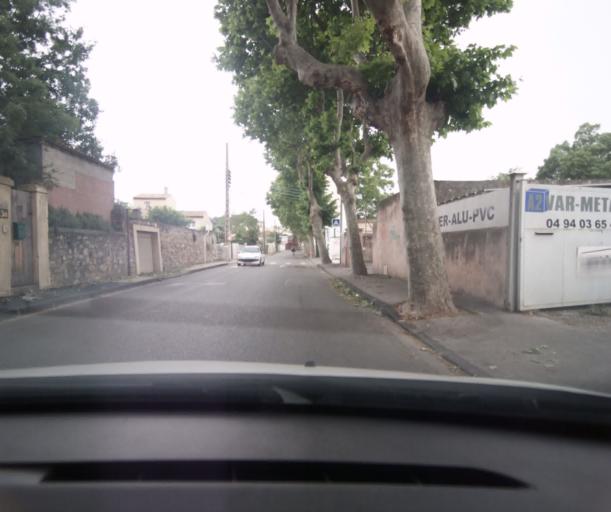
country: FR
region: Provence-Alpes-Cote d'Azur
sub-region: Departement du Var
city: Toulon
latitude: 43.1208
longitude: 5.9551
